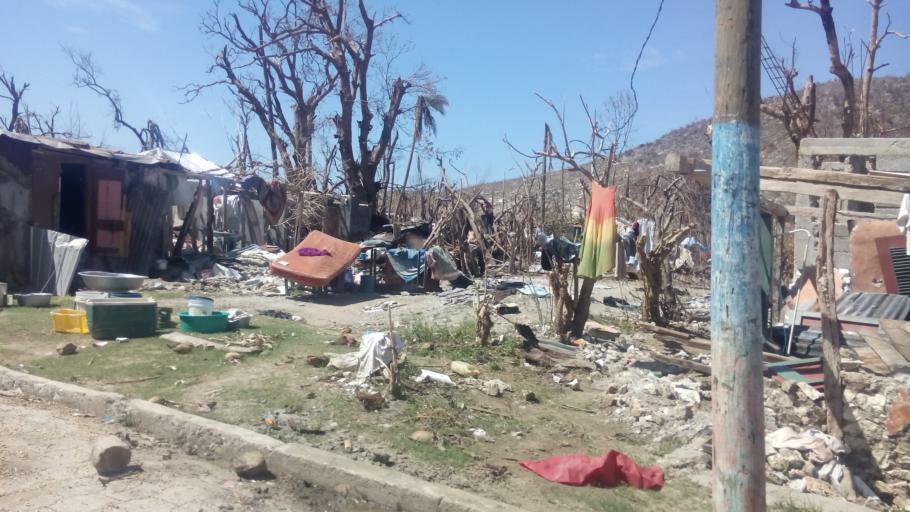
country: HT
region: Sud
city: Port-a-Piment
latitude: 18.2605
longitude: -74.0997
